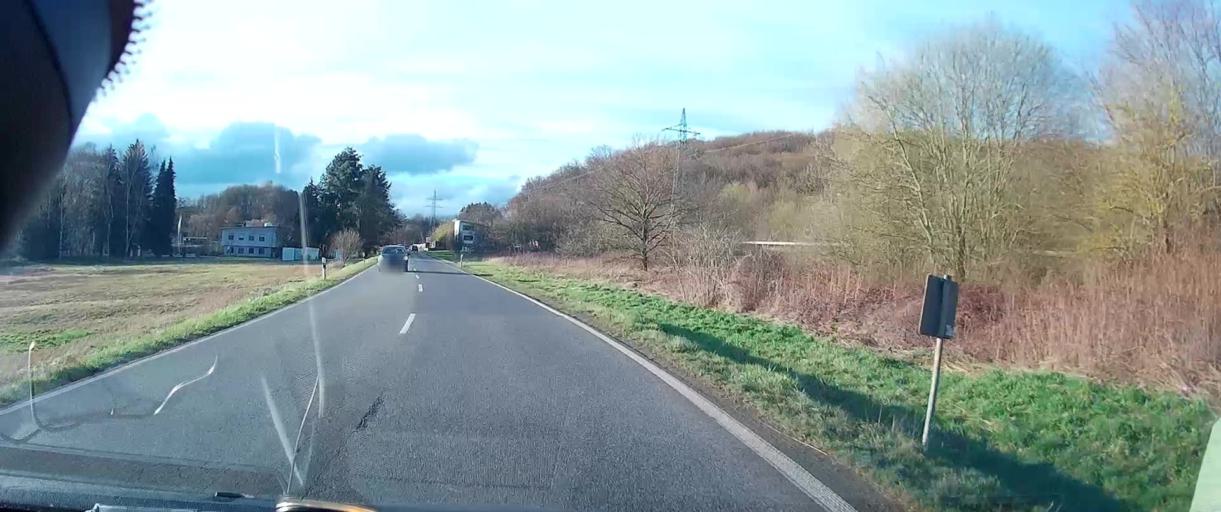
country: DE
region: Rheinland-Pfalz
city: Montabaur
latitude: 50.4494
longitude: 7.8157
